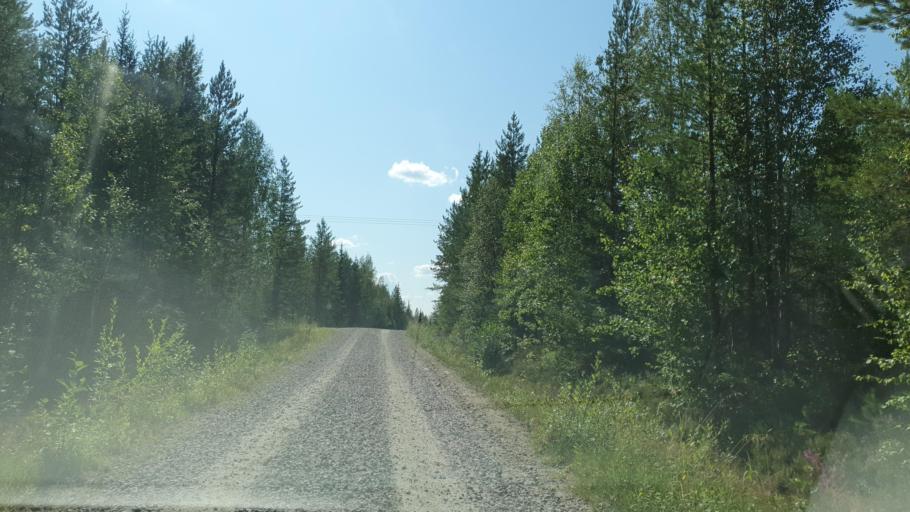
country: FI
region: Kainuu
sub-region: Kehys-Kainuu
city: Kuhmo
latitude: 64.0159
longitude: 29.6019
